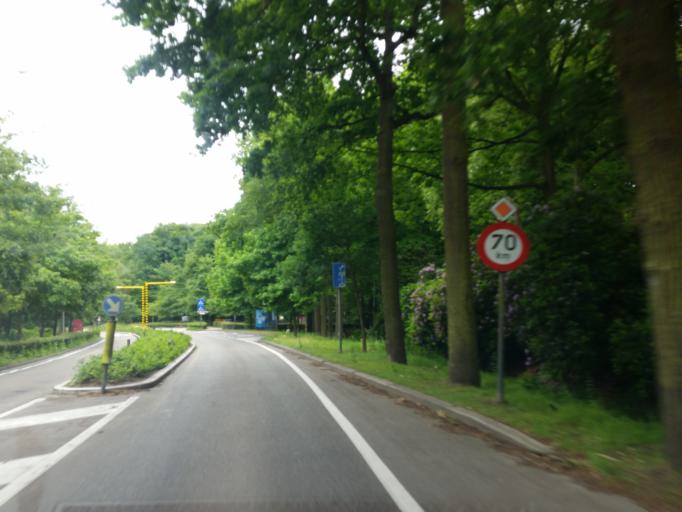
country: BE
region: Flanders
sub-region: Provincie Antwerpen
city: Brasschaat
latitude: 51.2866
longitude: 4.5031
